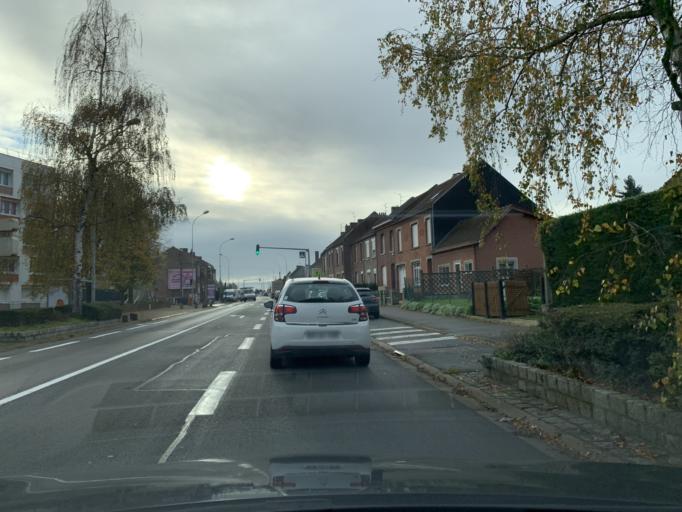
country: FR
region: Nord-Pas-de-Calais
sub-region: Departement du Nord
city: Lambres-lez-Douai
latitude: 50.3507
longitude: 3.0869
